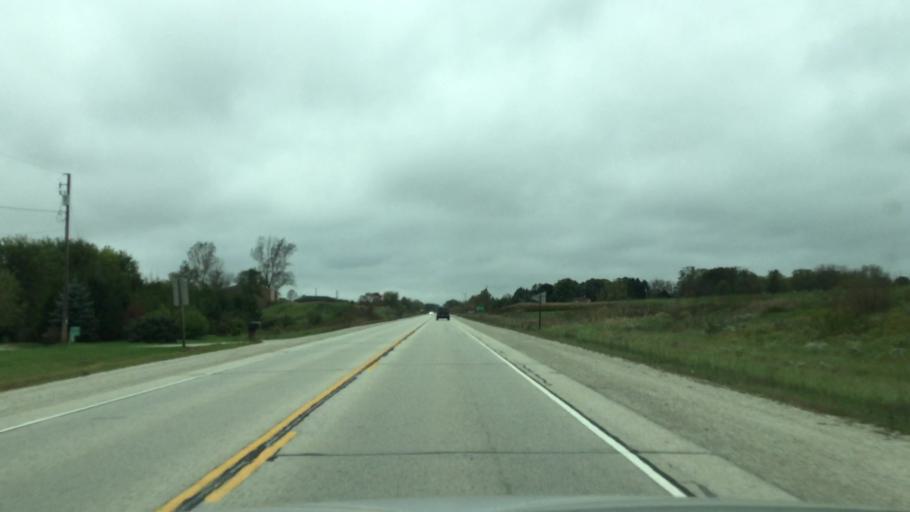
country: US
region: Wisconsin
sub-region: Racine County
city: Union Grove
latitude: 42.7376
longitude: -88.0231
